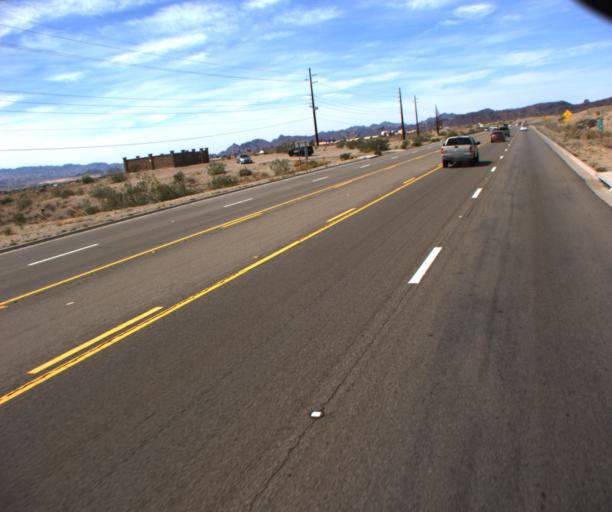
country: US
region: Arizona
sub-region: Mohave County
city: Desert Hills
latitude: 34.5243
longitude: -114.3495
